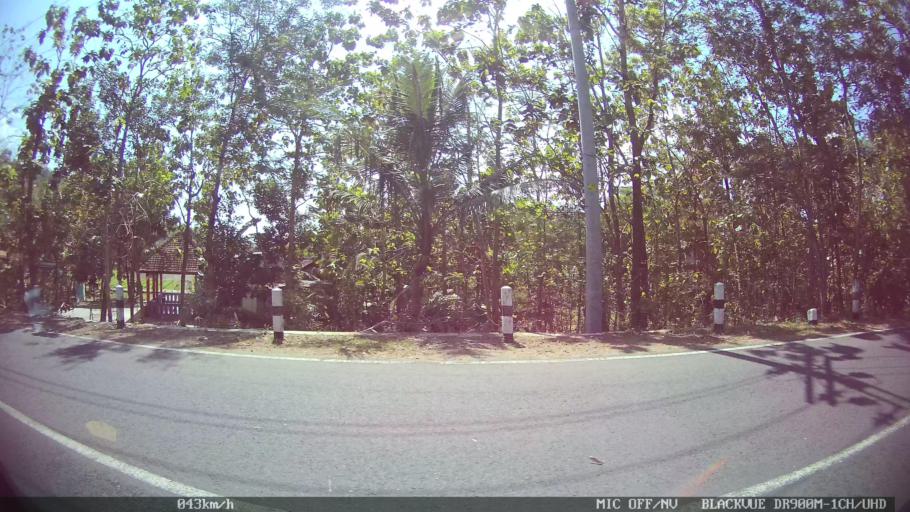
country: ID
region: Daerah Istimewa Yogyakarta
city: Pundong
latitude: -7.9593
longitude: 110.3780
